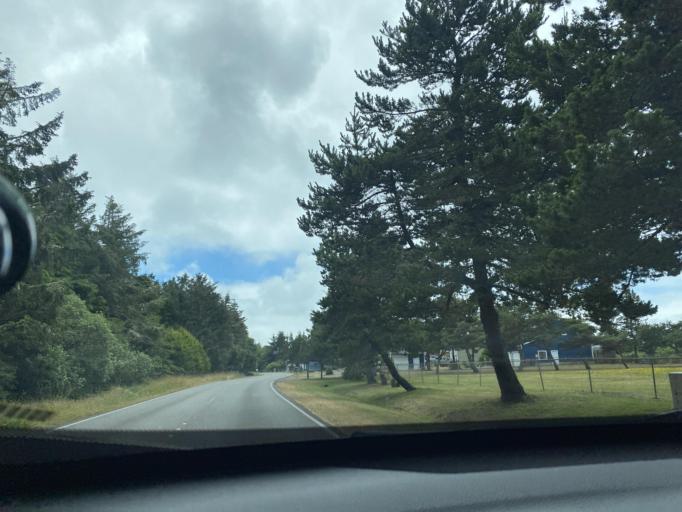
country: US
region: Washington
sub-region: Grays Harbor County
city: Ocean Shores
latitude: 46.9711
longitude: -124.1401
